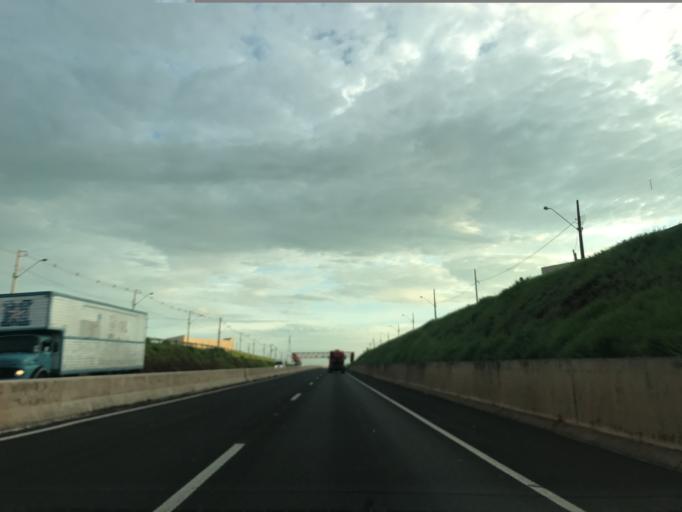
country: BR
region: Parana
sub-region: Maringa
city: Maringa
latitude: -23.3848
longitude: -51.9643
